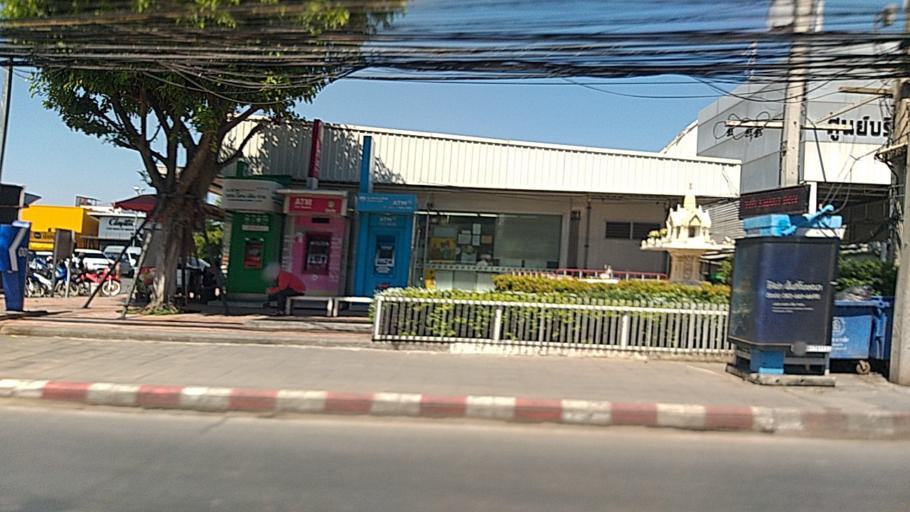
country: TH
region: Nakhon Ratchasima
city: Nakhon Ratchasima
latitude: 14.9796
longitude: 102.0817
